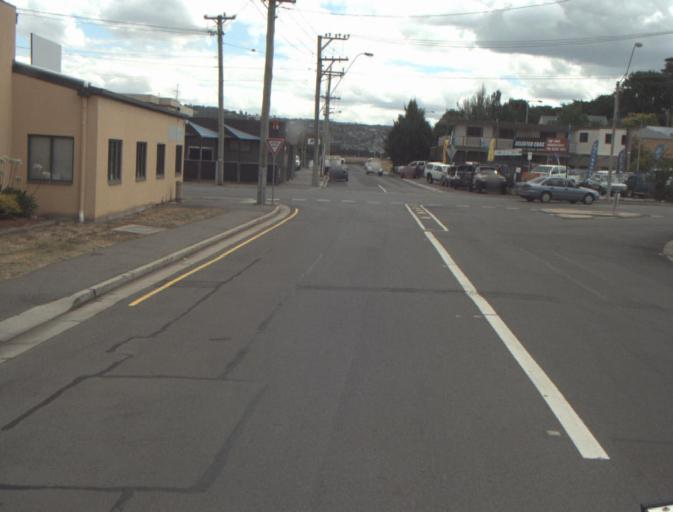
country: AU
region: Tasmania
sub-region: Launceston
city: Newnham
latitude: -41.4100
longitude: 147.1328
